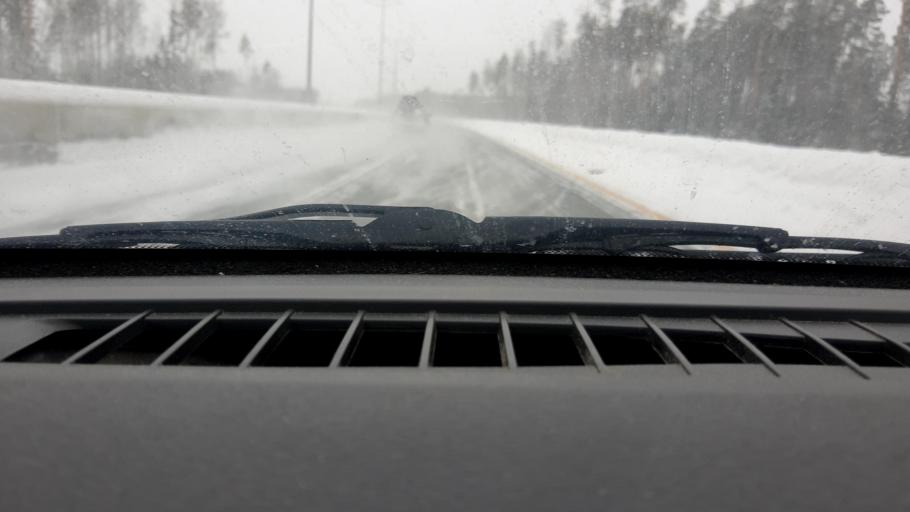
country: RU
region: Moskovskaya
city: Noginsk
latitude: 55.9287
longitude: 38.5017
